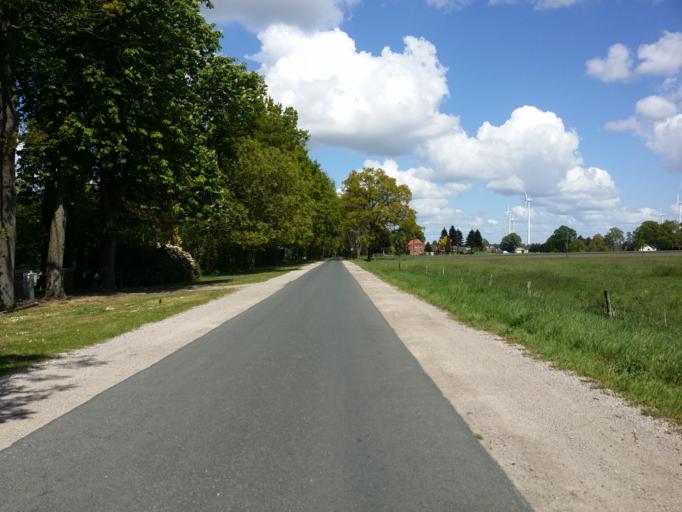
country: DE
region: Lower Saxony
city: Gross Ippener
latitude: 52.9991
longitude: 8.6062
